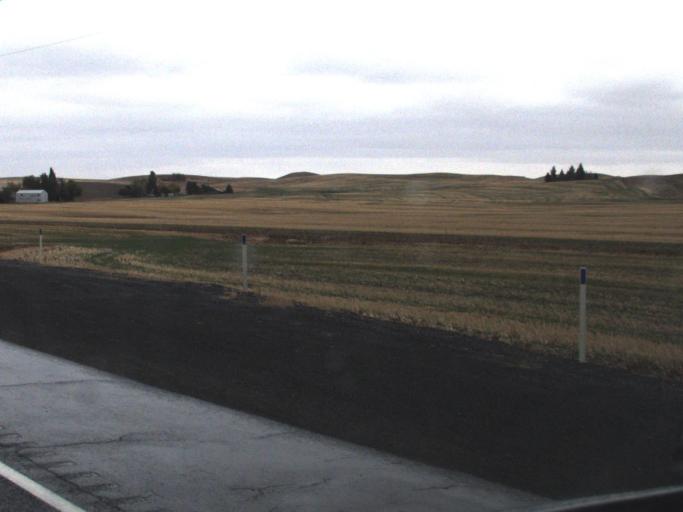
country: US
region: Washington
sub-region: Whitman County
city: Colfax
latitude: 46.7866
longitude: -117.3061
